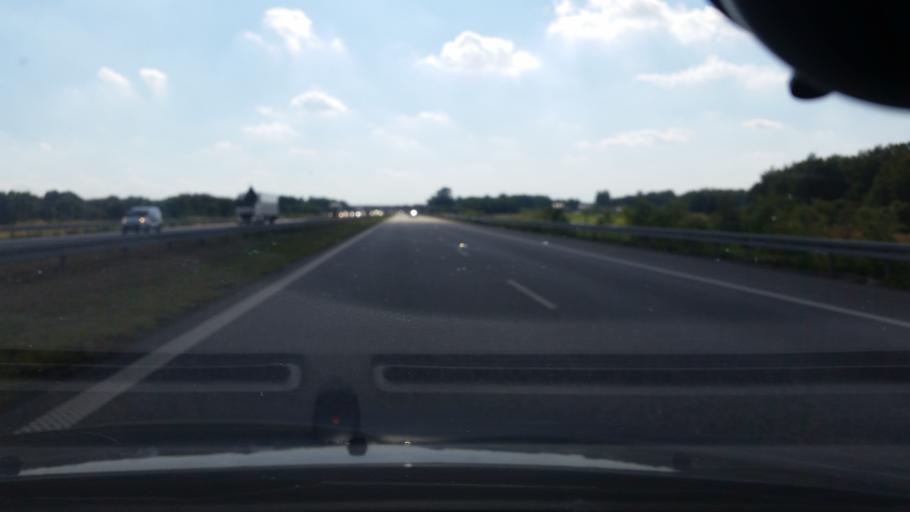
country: PL
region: Lodz Voivodeship
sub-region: powiat Lowicki
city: Bobrowniki
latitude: 52.0200
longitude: 19.9829
